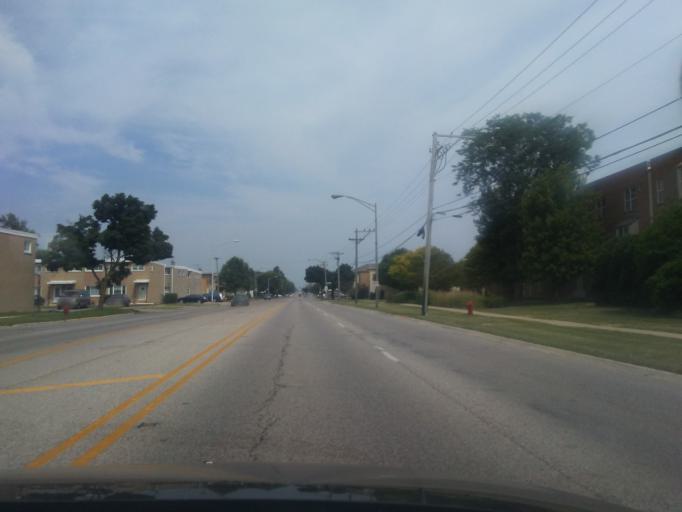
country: US
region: Illinois
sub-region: Cook County
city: Norridge
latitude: 41.9667
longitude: -87.8259
